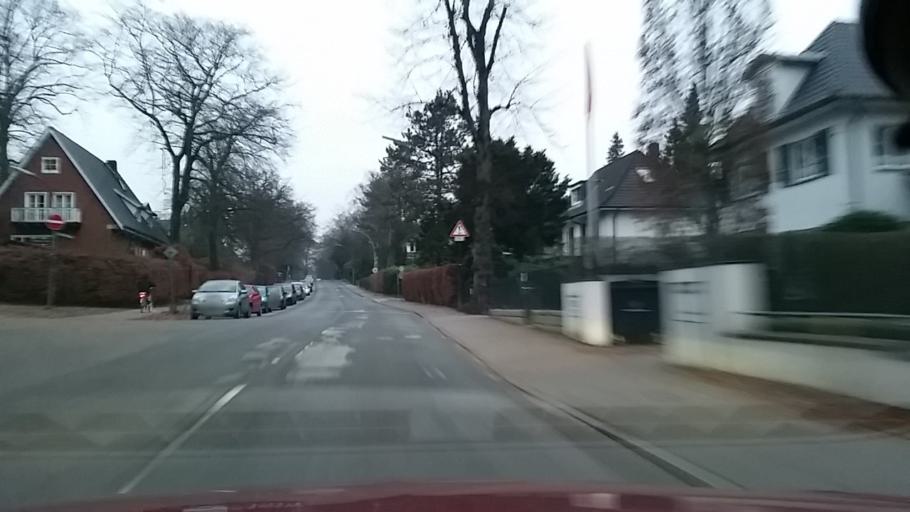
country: DE
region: Schleswig-Holstein
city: Halstenbek
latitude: 53.5645
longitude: 9.8121
